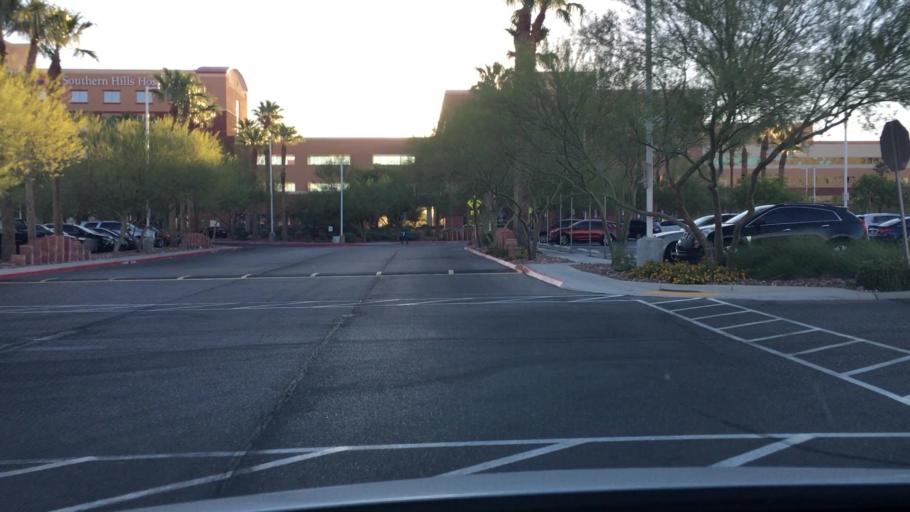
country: US
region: Nevada
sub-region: Clark County
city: Summerlin South
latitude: 36.0720
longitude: -115.2968
